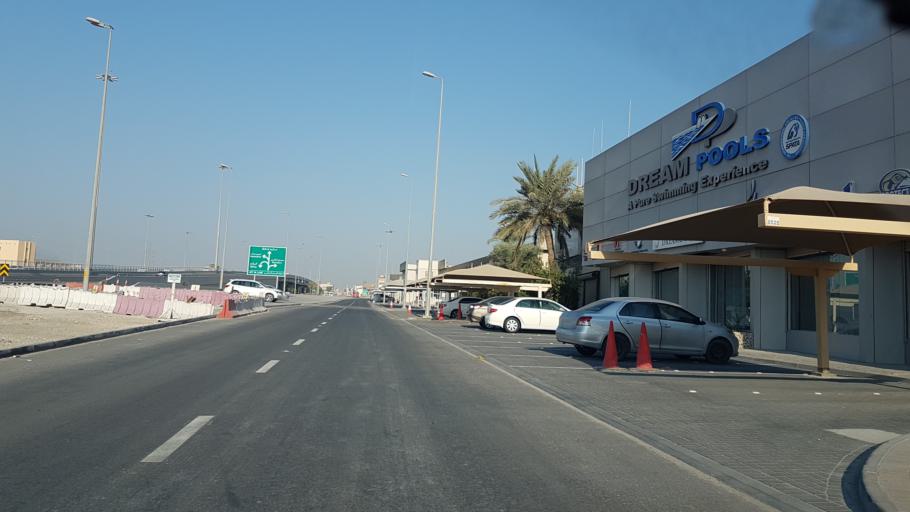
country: BH
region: Northern
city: Sitrah
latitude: 26.1283
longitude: 50.5986
